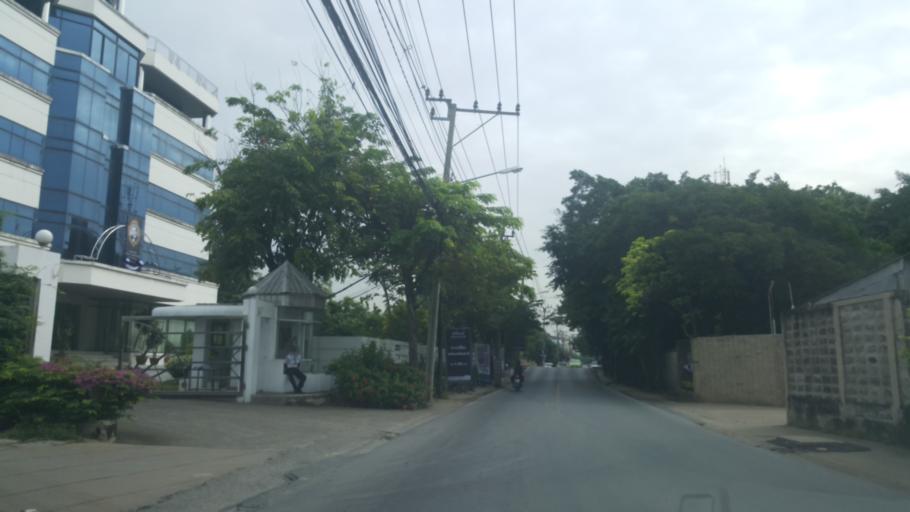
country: TH
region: Bangkok
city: Bang Khae
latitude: 13.6959
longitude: 100.3882
